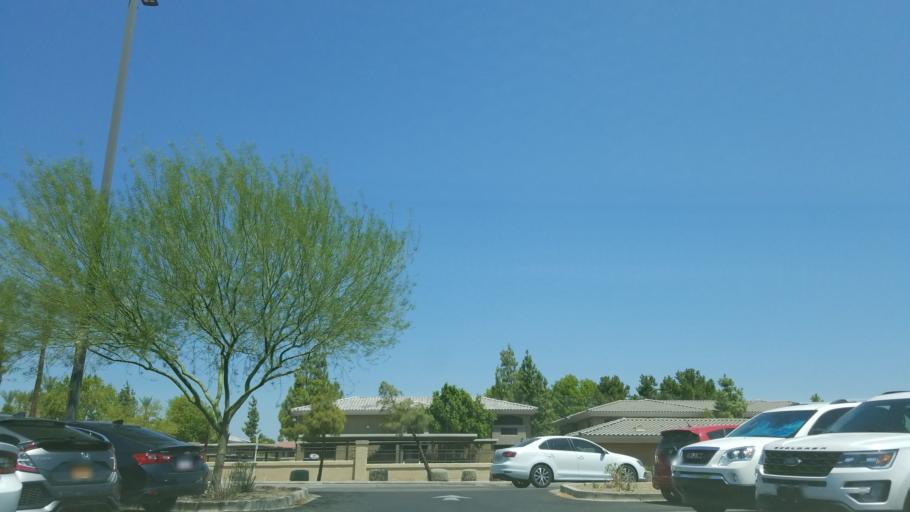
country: US
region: Arizona
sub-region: Maricopa County
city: Peoria
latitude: 33.6439
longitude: -112.2257
